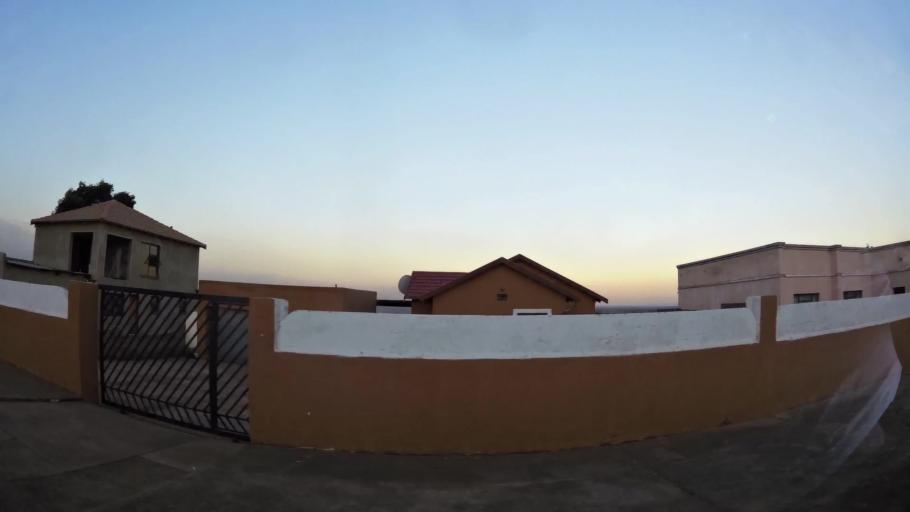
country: ZA
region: Gauteng
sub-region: West Rand District Municipality
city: Randfontein
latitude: -26.2055
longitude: 27.7197
